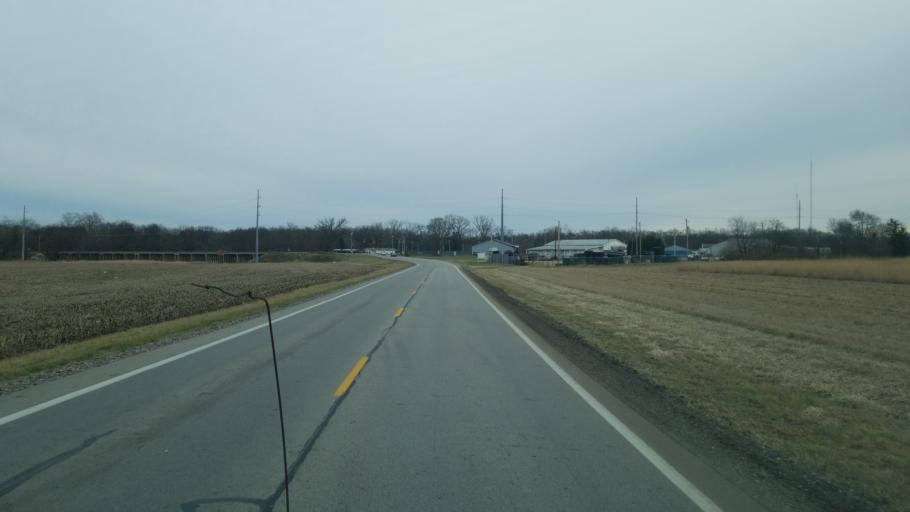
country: US
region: Ohio
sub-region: Pickaway County
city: Circleville
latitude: 39.6008
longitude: -82.9763
